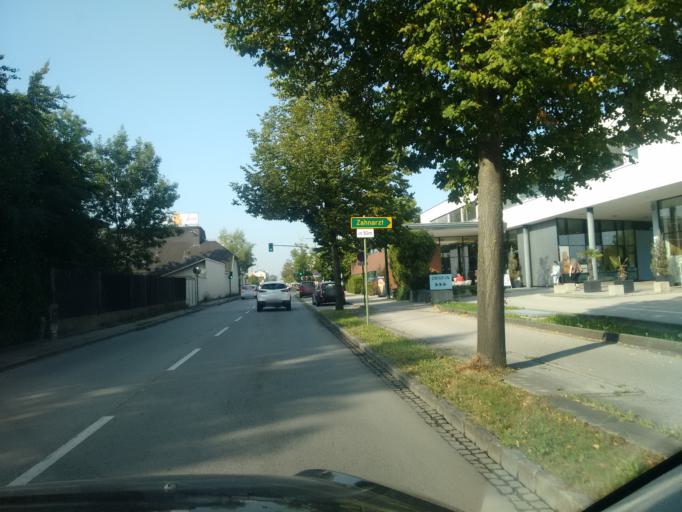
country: AT
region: Upper Austria
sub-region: Wels Stadt
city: Wels
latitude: 48.1699
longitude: 14.0463
